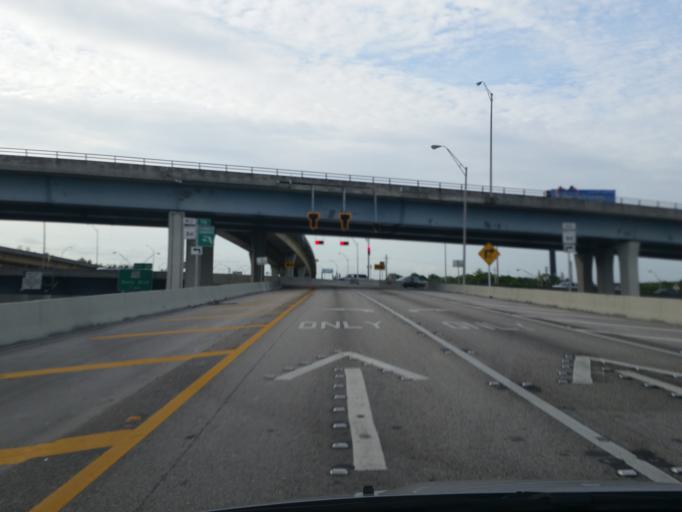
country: US
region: Florida
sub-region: Broward County
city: Melrose Park
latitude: 26.0878
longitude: -80.1679
